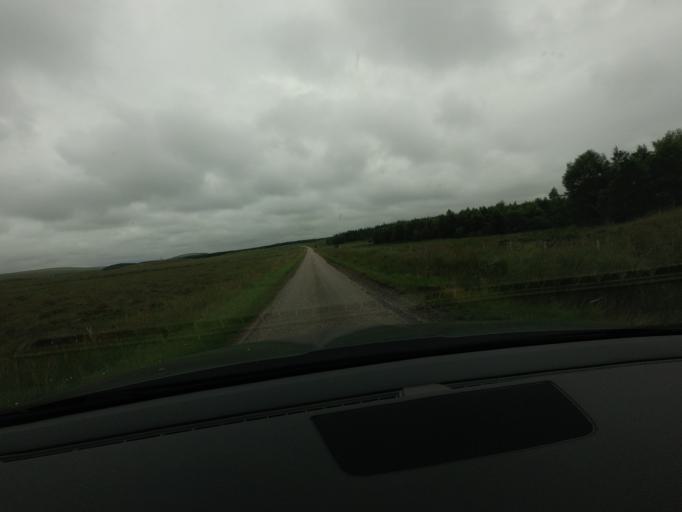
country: GB
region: Scotland
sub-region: Highland
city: Alness
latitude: 58.0961
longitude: -4.4217
